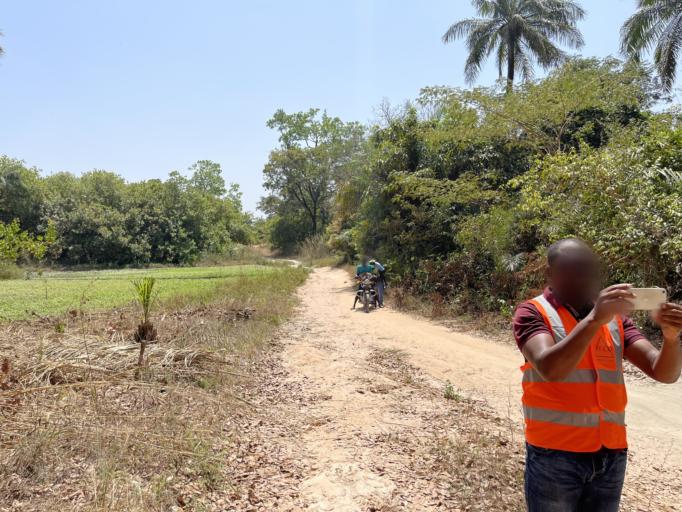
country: GW
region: Oio
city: Bissora
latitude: 12.4332
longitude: -15.6153
